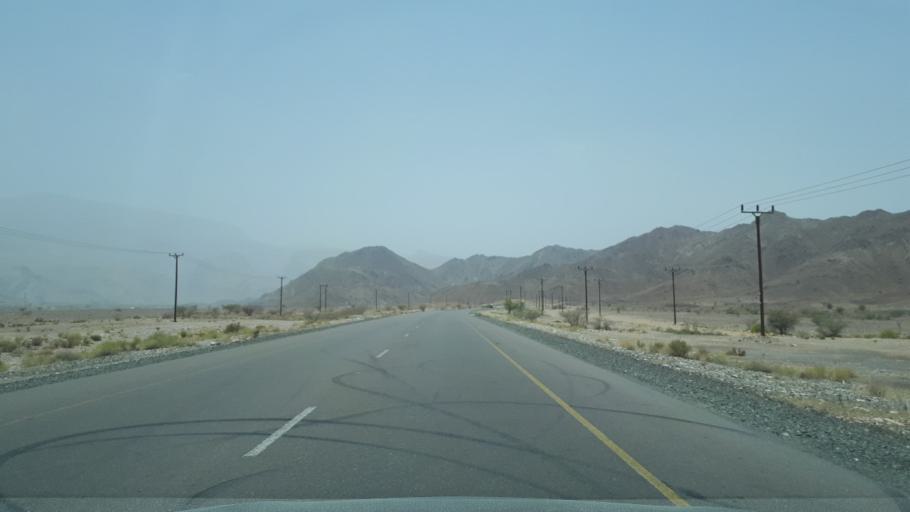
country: OM
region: Al Batinah
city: Rustaq
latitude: 23.4052
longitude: 57.2512
